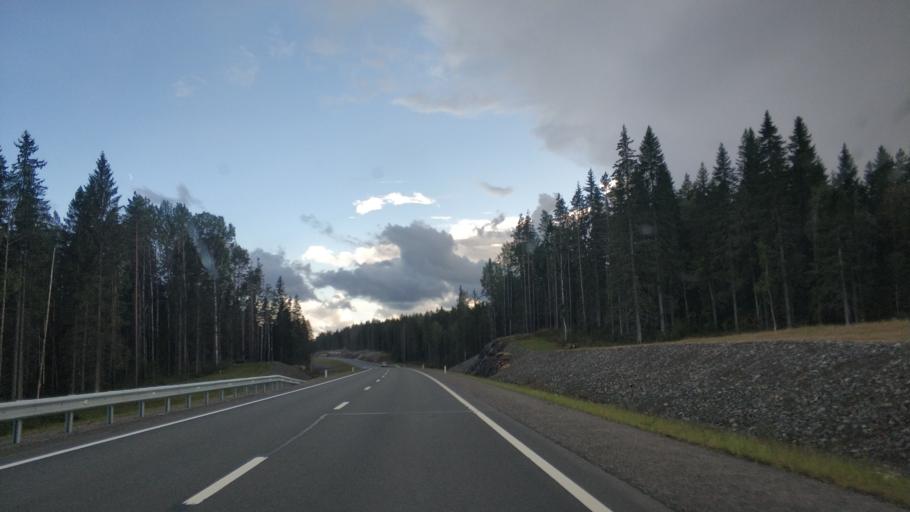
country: RU
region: Republic of Karelia
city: Lakhdenpokh'ya
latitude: 61.4197
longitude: 29.9633
